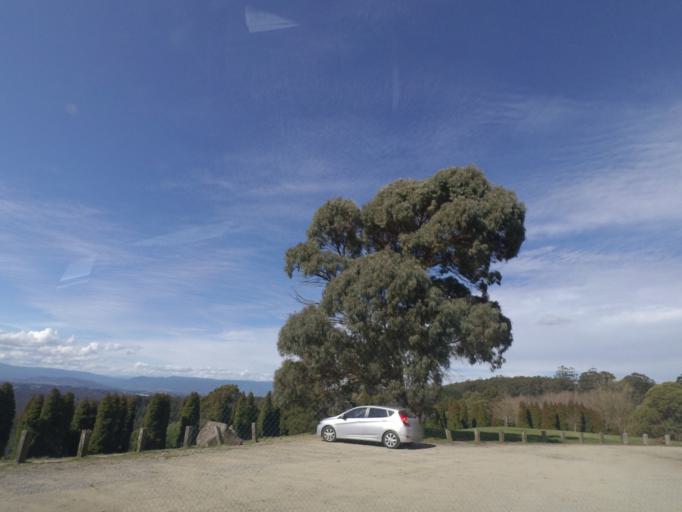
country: AU
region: Victoria
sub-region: Yarra Ranges
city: Olinda
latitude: -37.8600
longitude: 145.3824
